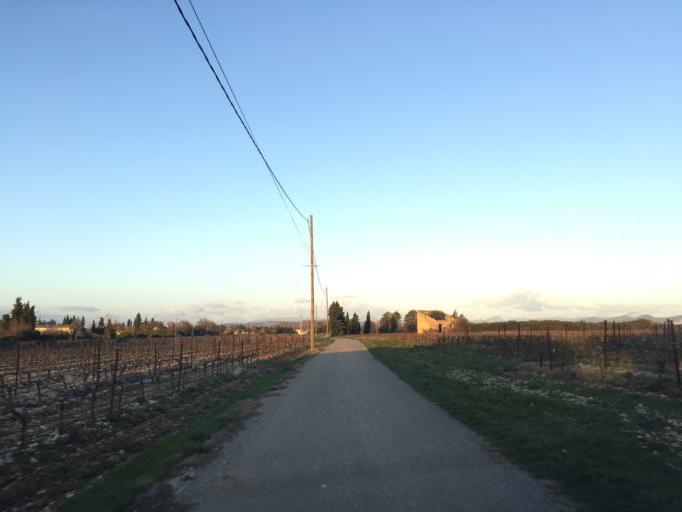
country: FR
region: Provence-Alpes-Cote d'Azur
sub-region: Departement du Vaucluse
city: Camaret-sur-Aigues
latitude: 44.1501
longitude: 4.8904
